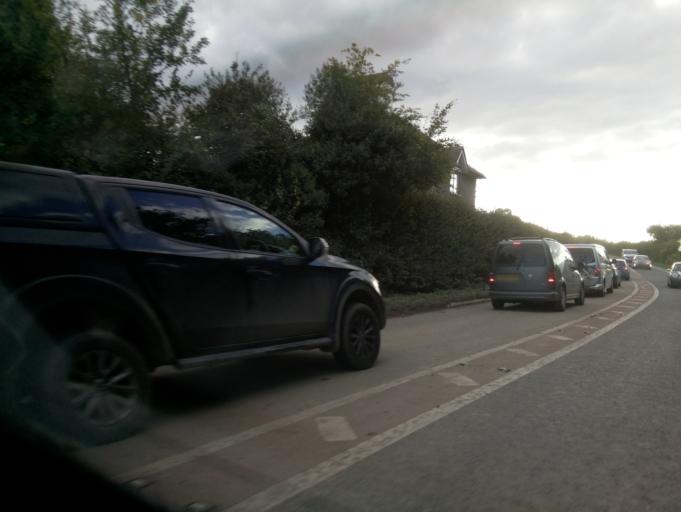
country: GB
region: England
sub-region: Herefordshire
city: Ocle Pychard
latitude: 52.0659
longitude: -2.5817
